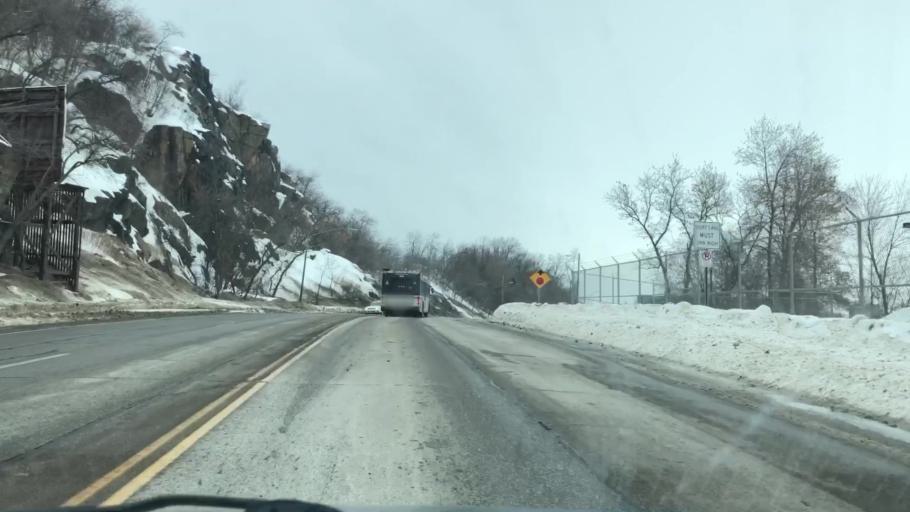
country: US
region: Minnesota
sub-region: Saint Louis County
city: Duluth
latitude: 46.7731
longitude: -92.1162
